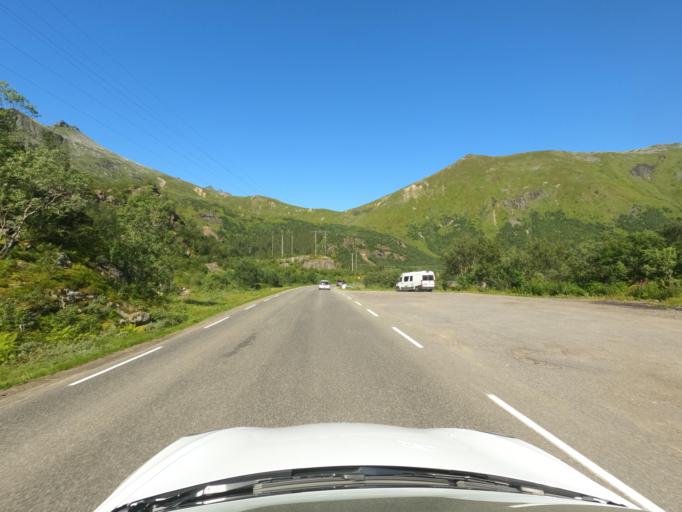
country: NO
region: Nordland
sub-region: Hadsel
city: Melbu
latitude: 68.3560
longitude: 14.7085
